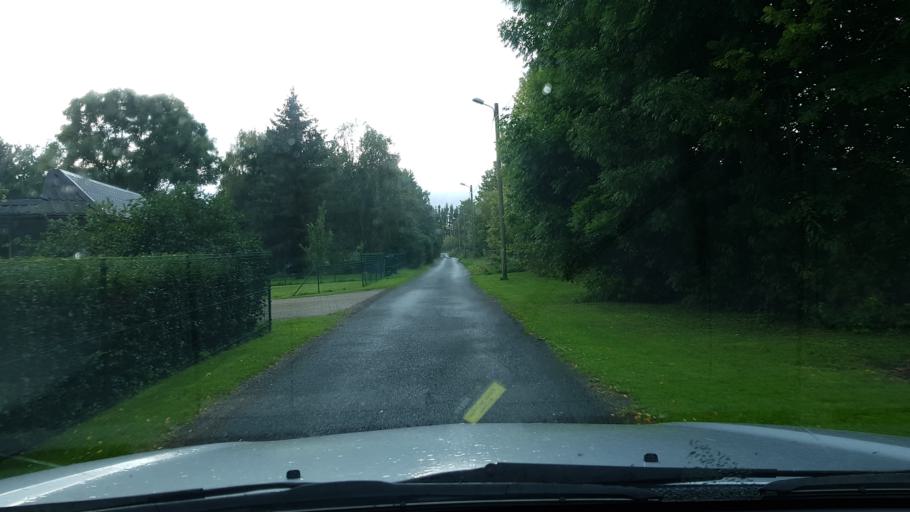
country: EE
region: Harju
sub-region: Joelaehtme vald
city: Loo
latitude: 59.4092
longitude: 24.9402
